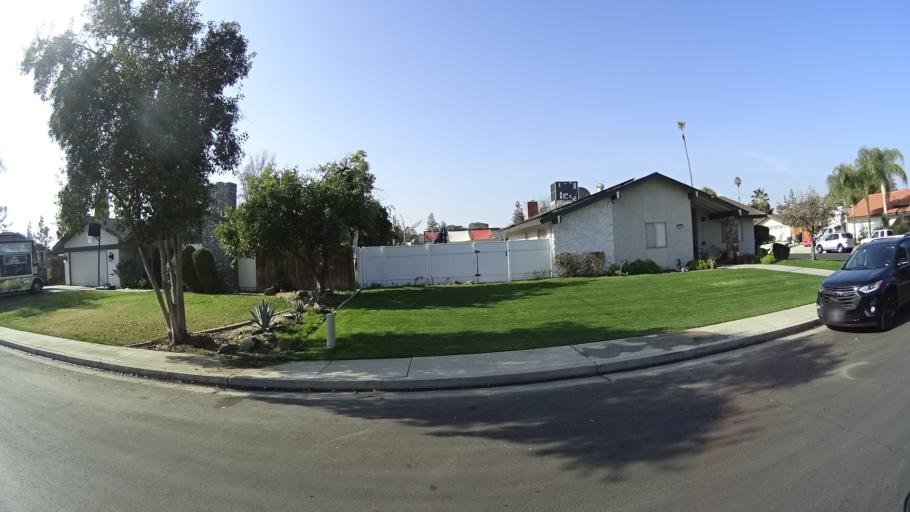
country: US
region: California
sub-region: Kern County
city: Greenacres
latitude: 35.3365
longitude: -119.0696
